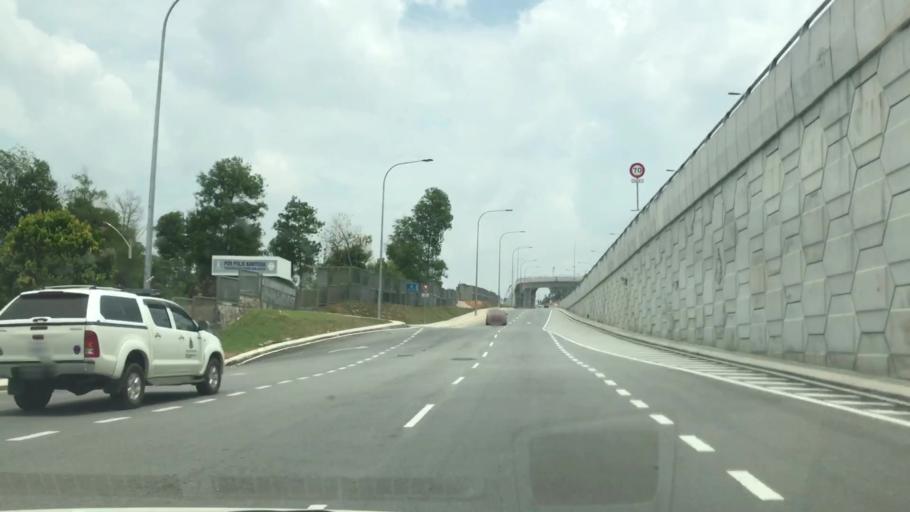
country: MY
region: Selangor
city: Kampong Baharu Balakong
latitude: 3.0492
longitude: 101.6799
